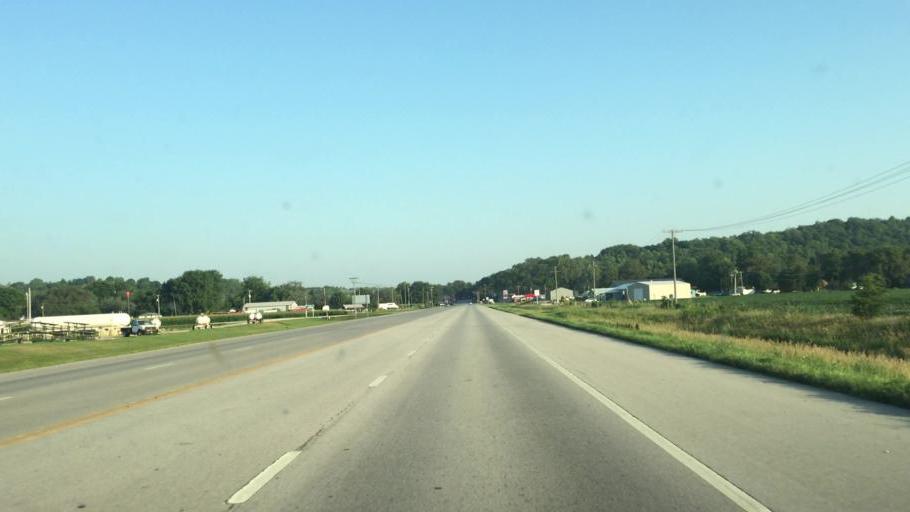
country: US
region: Kansas
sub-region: Doniphan County
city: Wathena
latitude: 39.7554
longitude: -94.9377
